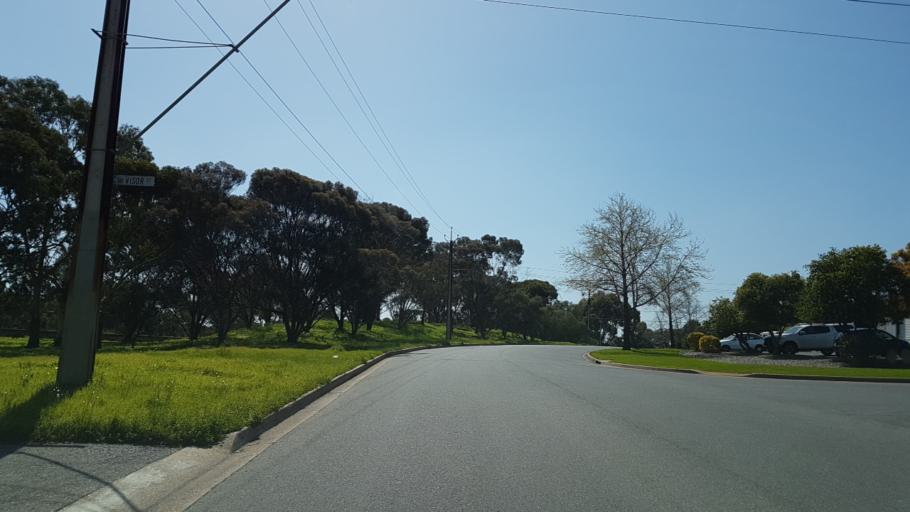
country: AU
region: South Australia
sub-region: Tea Tree Gully
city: Modbury
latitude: -34.8460
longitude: 138.6785
